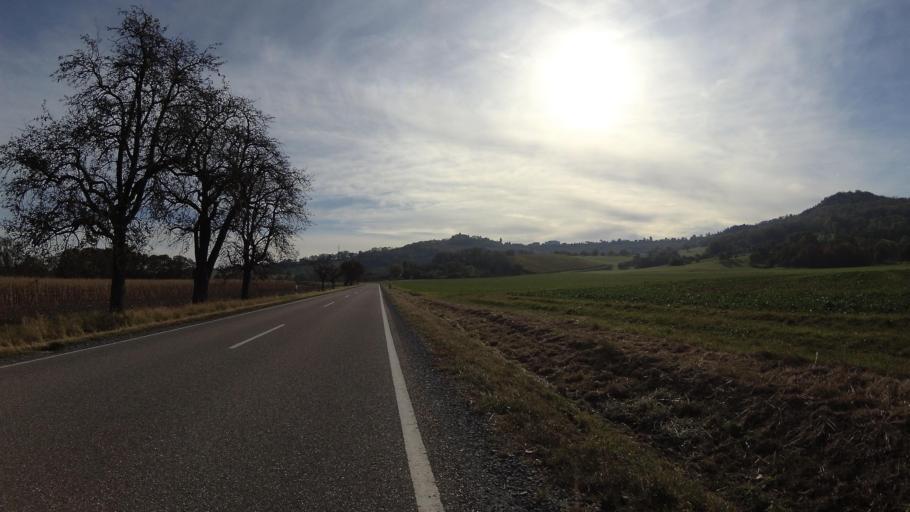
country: DE
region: Baden-Wuerttemberg
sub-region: Regierungsbezirk Stuttgart
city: Waldenburg
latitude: 49.2023
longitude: 9.6303
